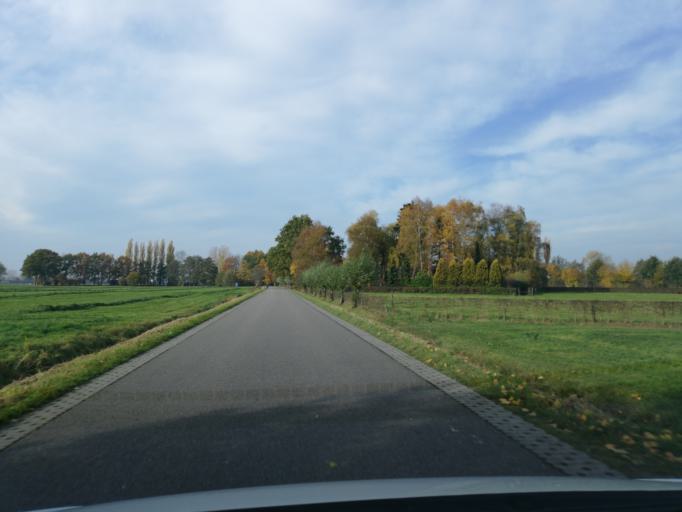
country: NL
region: Gelderland
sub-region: Gemeente Apeldoorn
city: Apeldoorn
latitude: 52.2439
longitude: 6.0245
